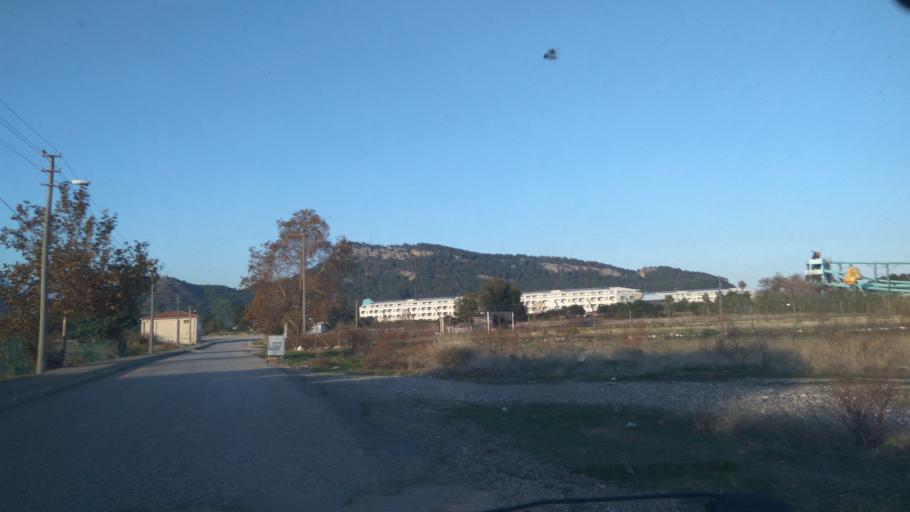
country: TR
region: Antalya
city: Kemer
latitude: 36.5628
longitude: 30.5715
